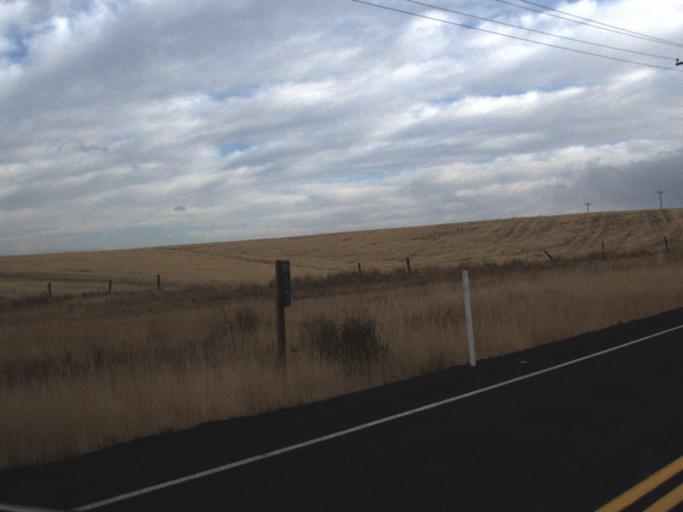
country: US
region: Washington
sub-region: Lincoln County
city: Davenport
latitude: 47.8619
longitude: -118.2442
